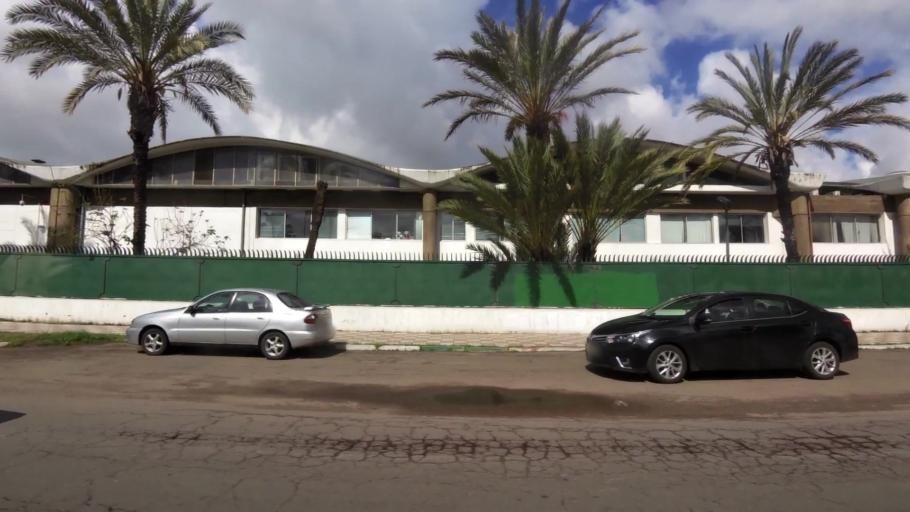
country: MA
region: Grand Casablanca
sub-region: Nouaceur
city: Bouskoura
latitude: 33.5238
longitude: -7.6516
